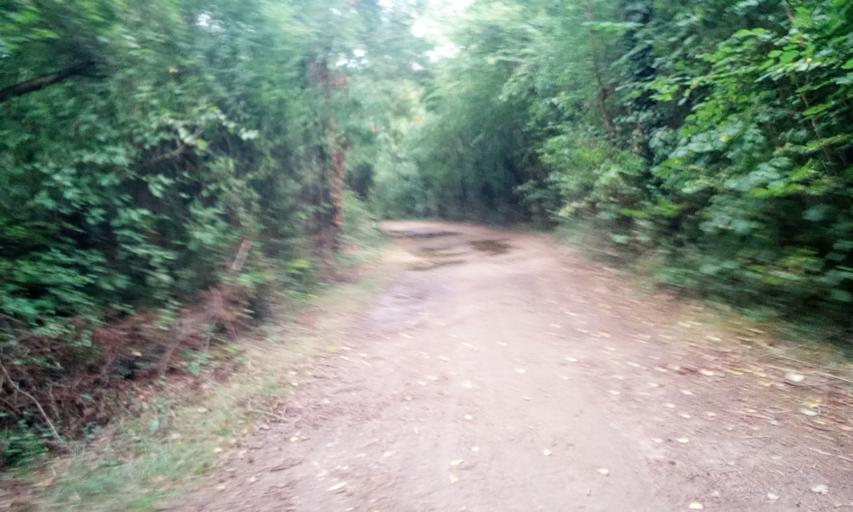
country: FR
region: Lower Normandy
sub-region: Departement du Calvados
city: Cagny
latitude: 49.1087
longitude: -0.2480
